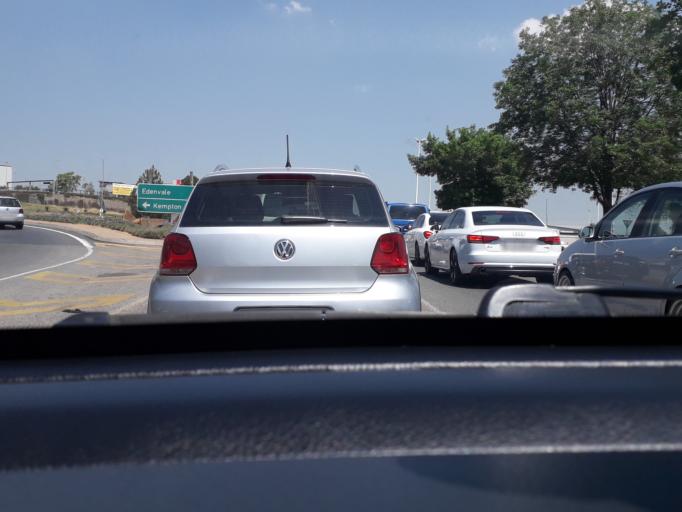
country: ZA
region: Gauteng
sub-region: City of Johannesburg Metropolitan Municipality
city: Modderfontein
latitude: -26.1182
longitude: 28.1376
